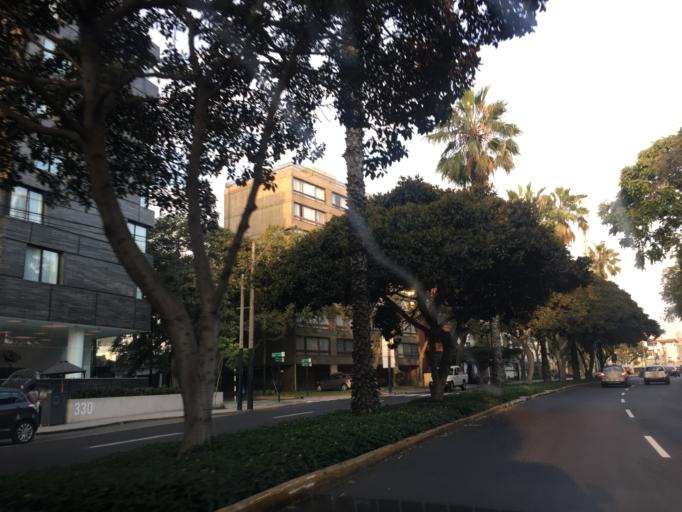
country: PE
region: Lima
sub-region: Lima
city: San Isidro
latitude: -12.1074
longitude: -77.0361
